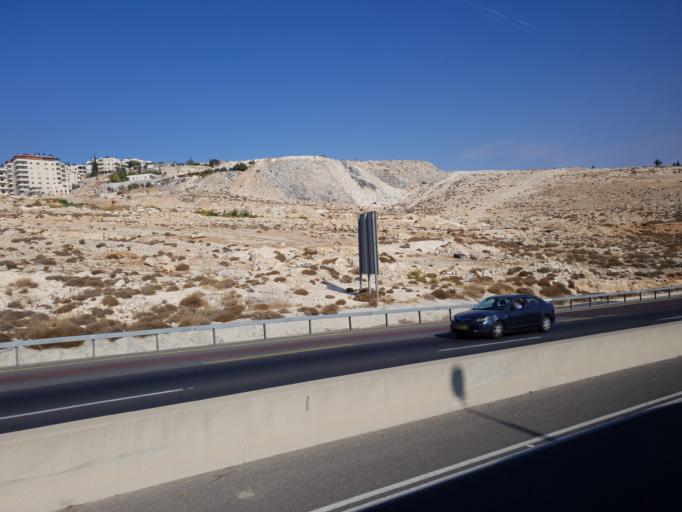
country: PS
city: Az Za`ayyim
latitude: 31.7847
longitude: 35.2696
